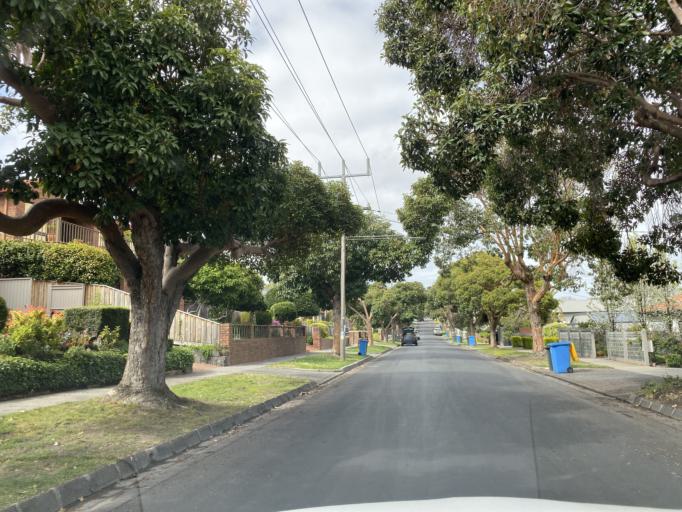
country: AU
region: Victoria
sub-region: Boroondara
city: Ashburton
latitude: -37.8504
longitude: 145.0870
